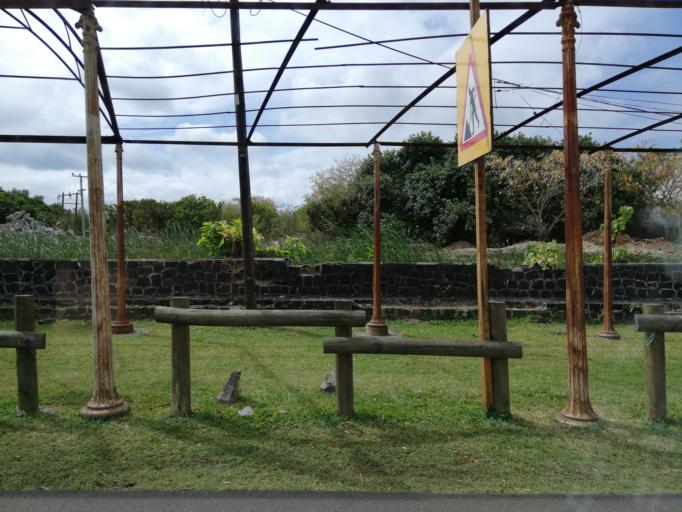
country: MU
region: Port Louis
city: Port Louis
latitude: -20.1571
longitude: 57.4869
